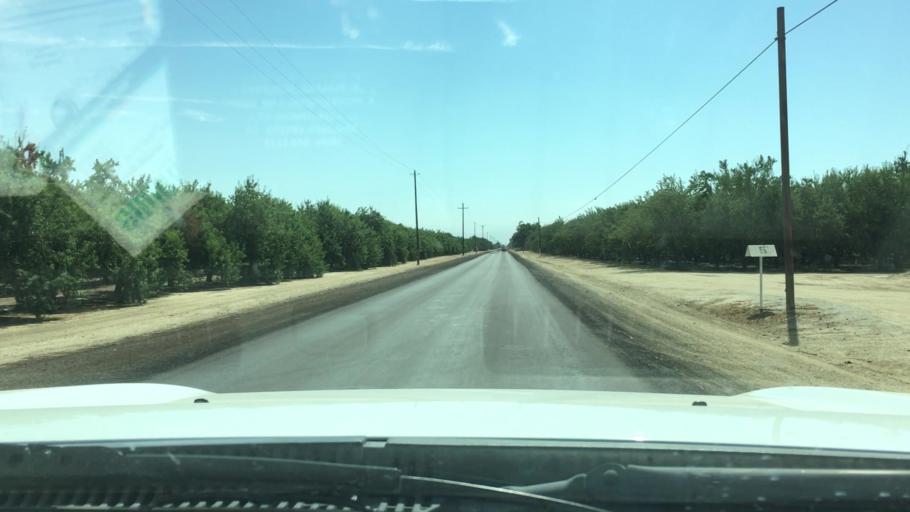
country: US
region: California
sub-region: Kern County
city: Wasco
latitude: 35.5290
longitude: -119.3455
